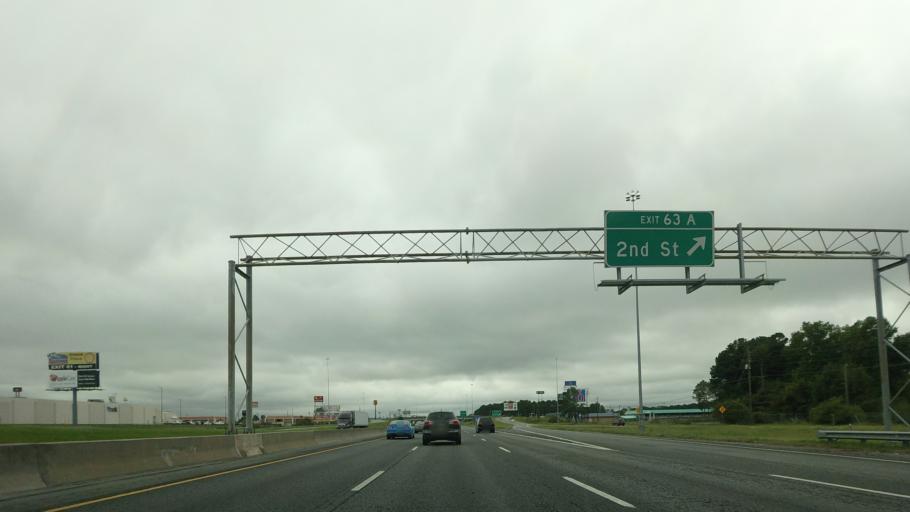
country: US
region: Georgia
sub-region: Tift County
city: Tifton
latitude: 31.4618
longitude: -83.5301
